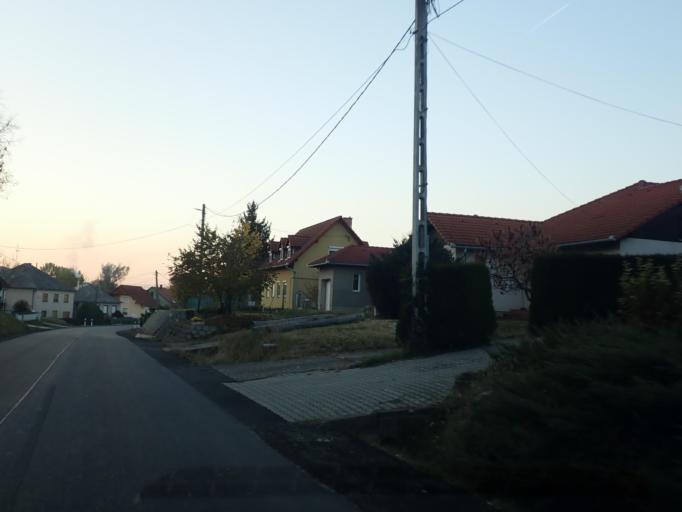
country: HU
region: Baranya
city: Kozarmisleny
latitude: 46.0281
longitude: 18.3930
